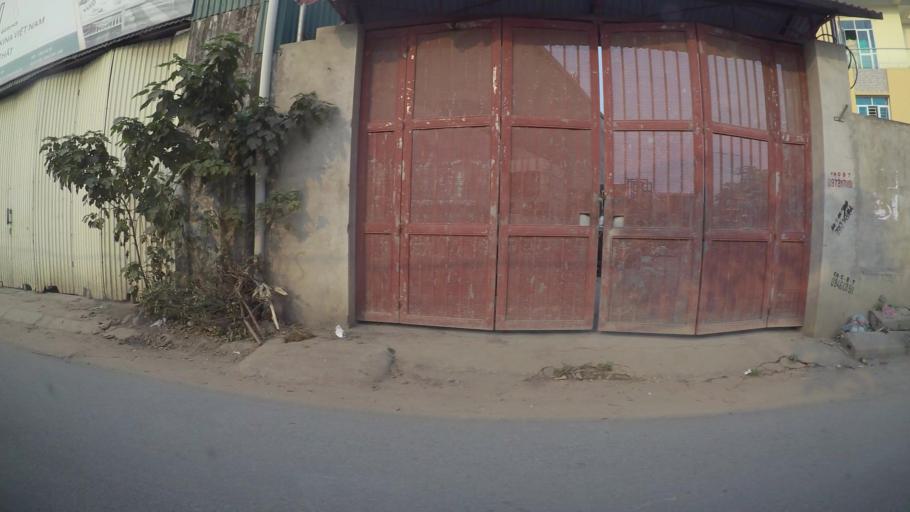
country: VN
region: Ha Noi
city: Ha Dong
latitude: 20.9998
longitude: 105.7422
